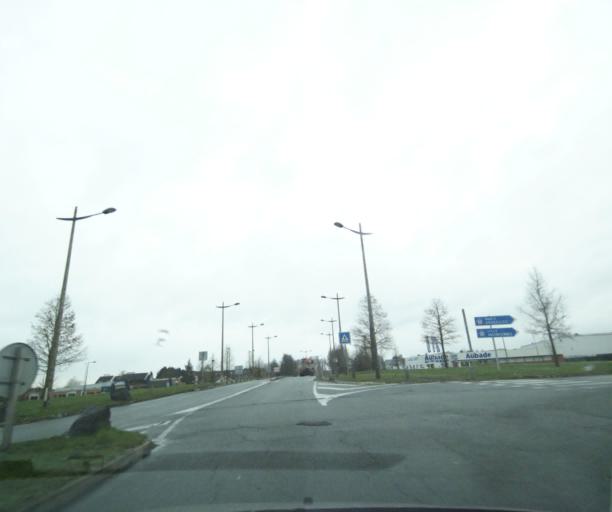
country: FR
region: Nord-Pas-de-Calais
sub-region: Departement du Nord
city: Prouvy
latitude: 50.3337
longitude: 3.4567
